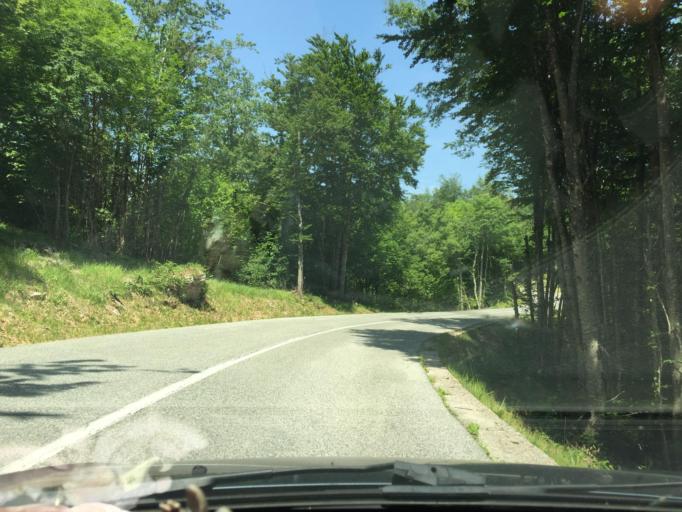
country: HR
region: Primorsko-Goranska
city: Matulji
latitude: 45.4102
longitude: 14.2509
